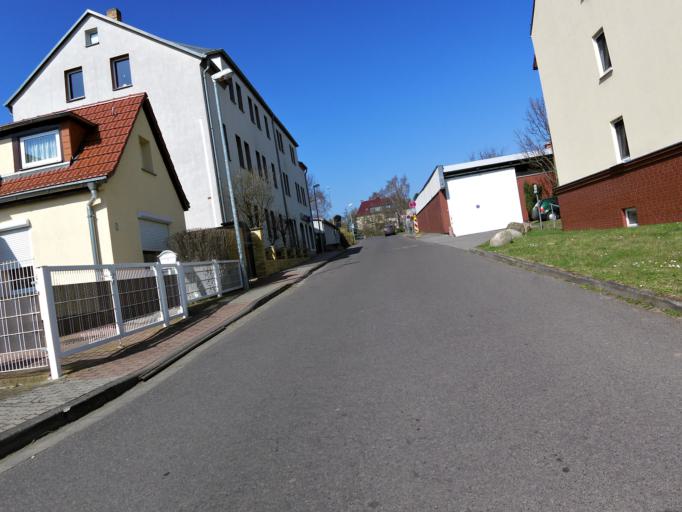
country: DE
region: Saxony
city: Leipzig
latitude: 51.3779
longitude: 12.3025
